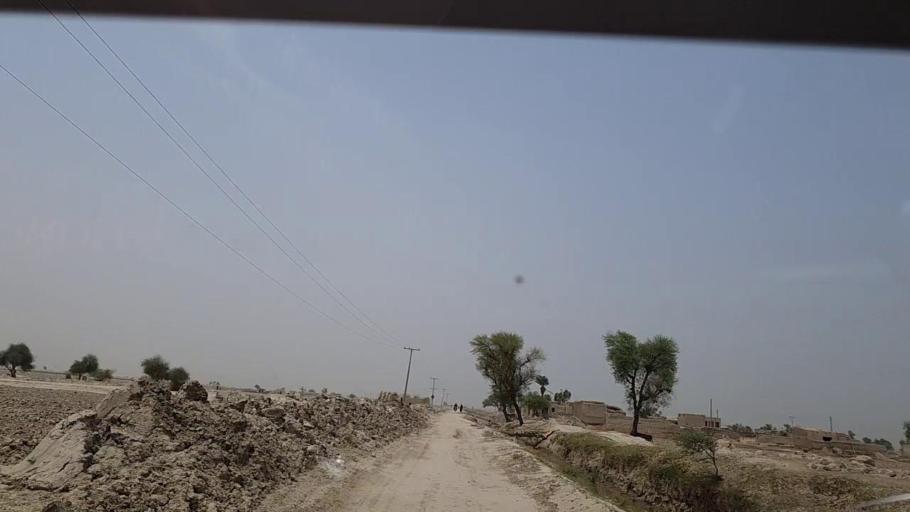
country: PK
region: Sindh
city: Khairpur Nathan Shah
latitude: 27.0517
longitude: 67.6192
